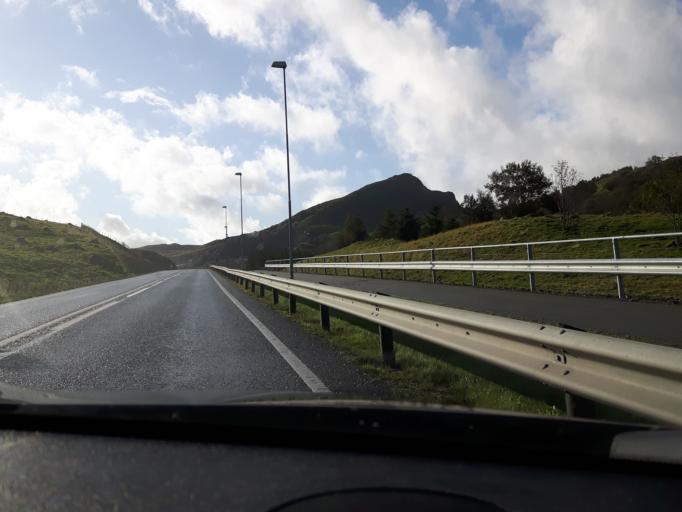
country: NO
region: Rogaland
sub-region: Gjesdal
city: Algard
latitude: 58.7609
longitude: 5.9001
